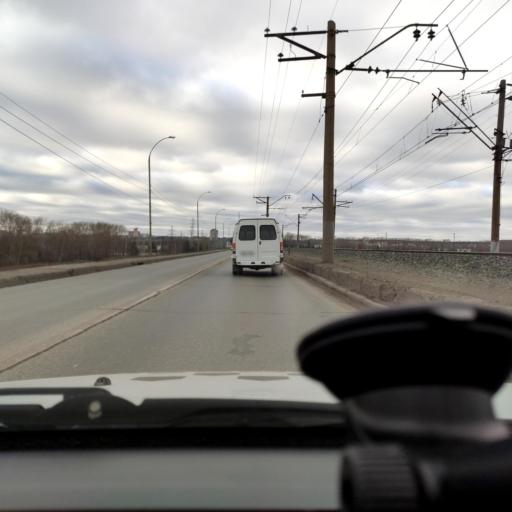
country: RU
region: Perm
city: Perm
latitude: 58.1146
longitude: 56.3605
